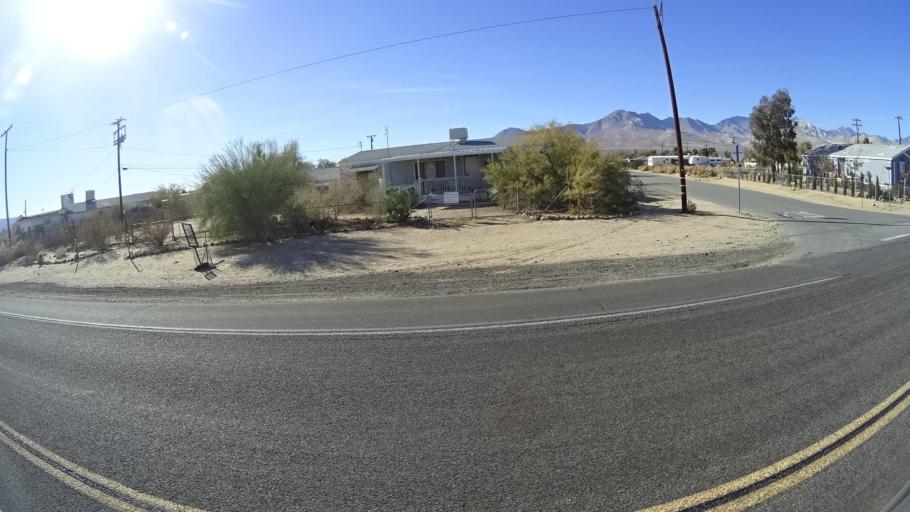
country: US
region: California
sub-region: Kern County
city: Inyokern
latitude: 35.6419
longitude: -117.8109
